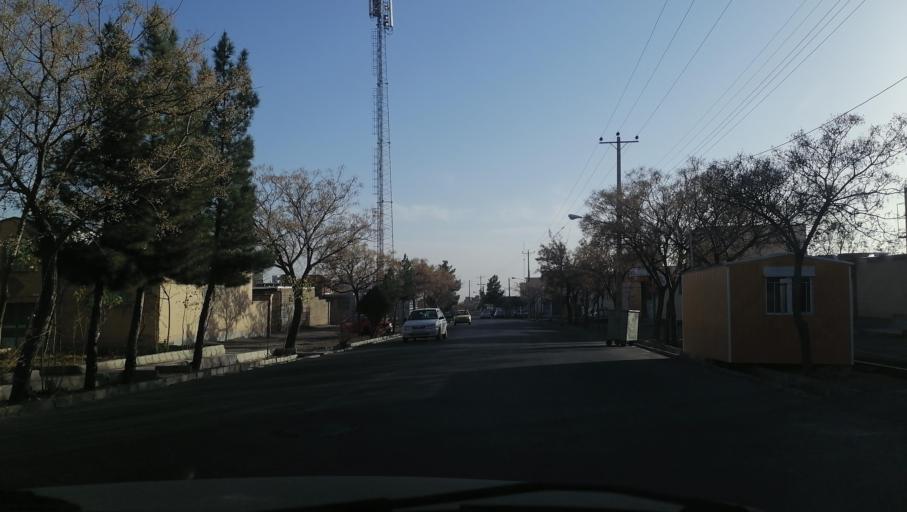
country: IR
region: Razavi Khorasan
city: Sabzevar
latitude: 36.2889
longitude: 57.6763
